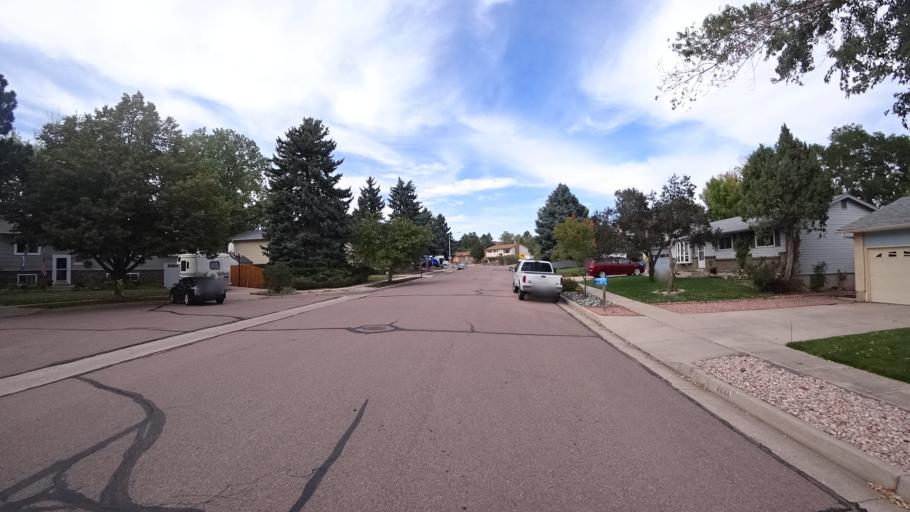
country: US
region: Colorado
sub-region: El Paso County
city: Cimarron Hills
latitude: 38.9009
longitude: -104.7704
